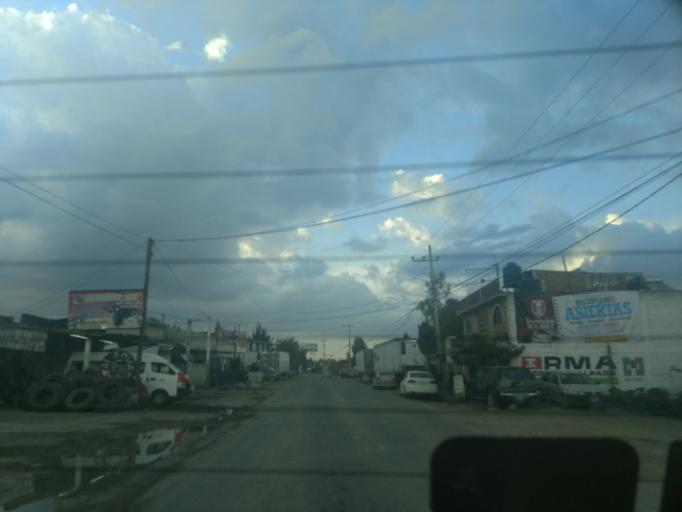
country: MX
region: Mexico
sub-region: Cuautitlan
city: Barrio Tlatenco
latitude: 19.7527
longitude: -99.2008
